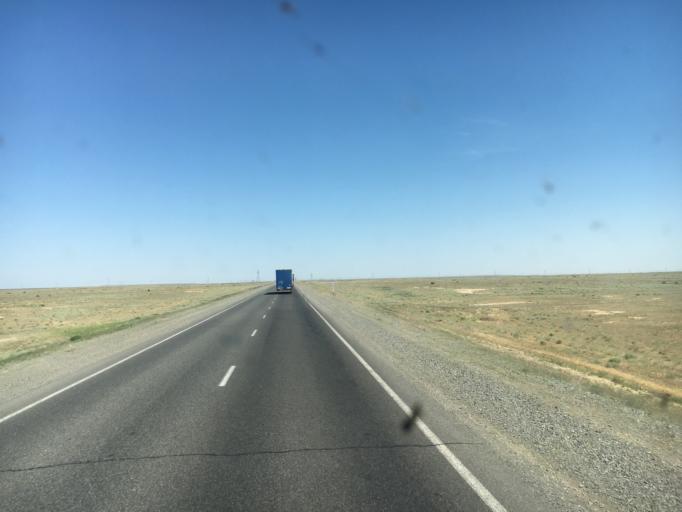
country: KZ
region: Qyzylorda
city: Aral
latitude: 47.0643
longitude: 61.5190
